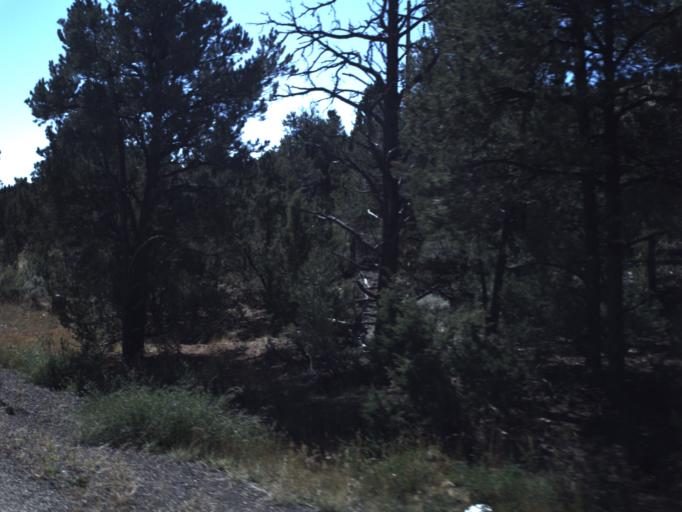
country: US
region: Utah
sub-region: Wayne County
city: Loa
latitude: 37.9273
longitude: -111.4277
